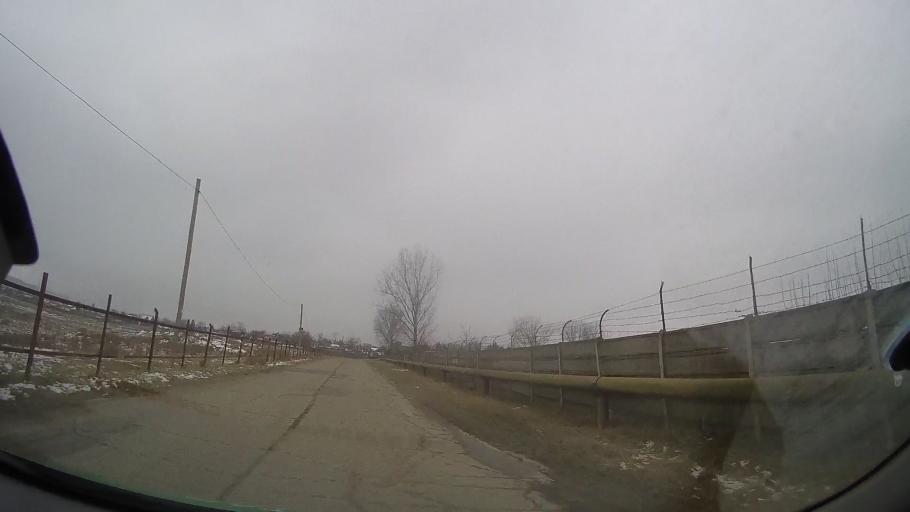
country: RO
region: Vaslui
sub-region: Municipiul Barlad
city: Barlad
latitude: 46.2393
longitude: 27.6820
